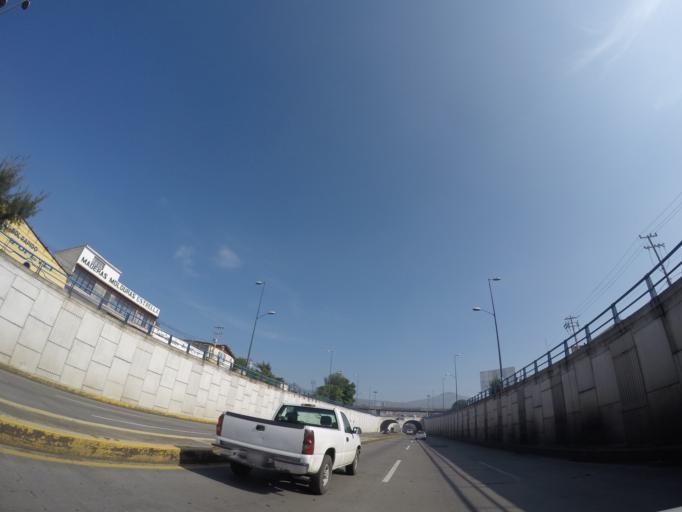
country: MX
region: Michoacan
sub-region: Morelia
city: San Antonio
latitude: 19.6982
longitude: -101.2425
